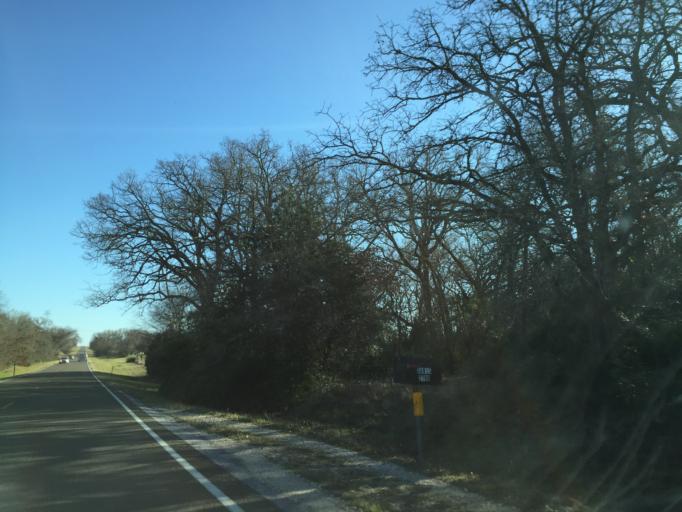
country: US
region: Texas
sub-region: Bastrop County
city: Elgin
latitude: 30.4226
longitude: -97.2587
